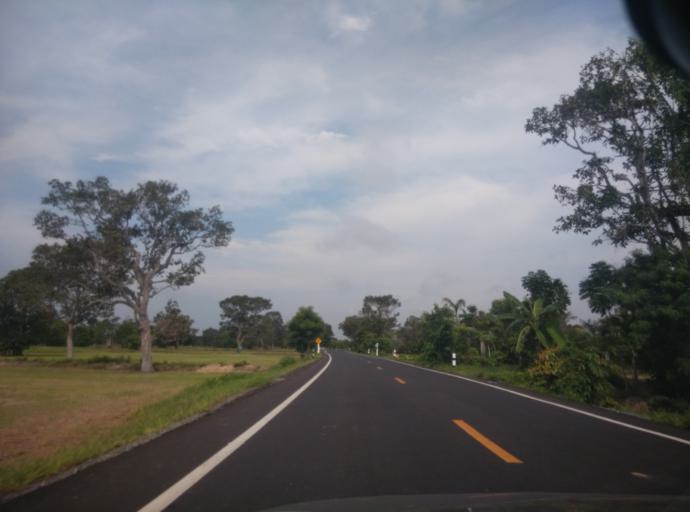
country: TH
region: Sisaket
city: Si Sa Ket
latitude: 15.1219
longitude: 104.2360
